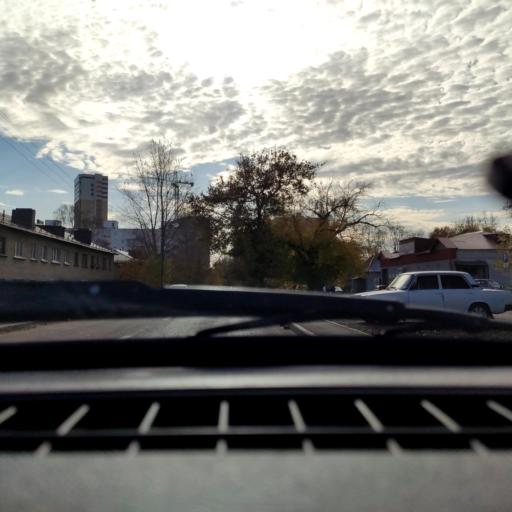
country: RU
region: Bashkortostan
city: Ufa
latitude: 54.8096
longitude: 56.1264
